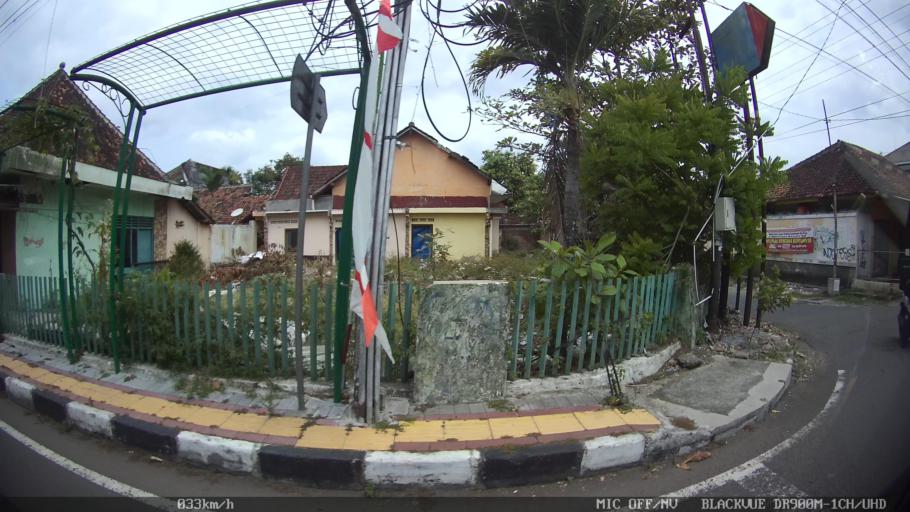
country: ID
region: Daerah Istimewa Yogyakarta
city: Yogyakarta
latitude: -7.7986
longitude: 110.3883
